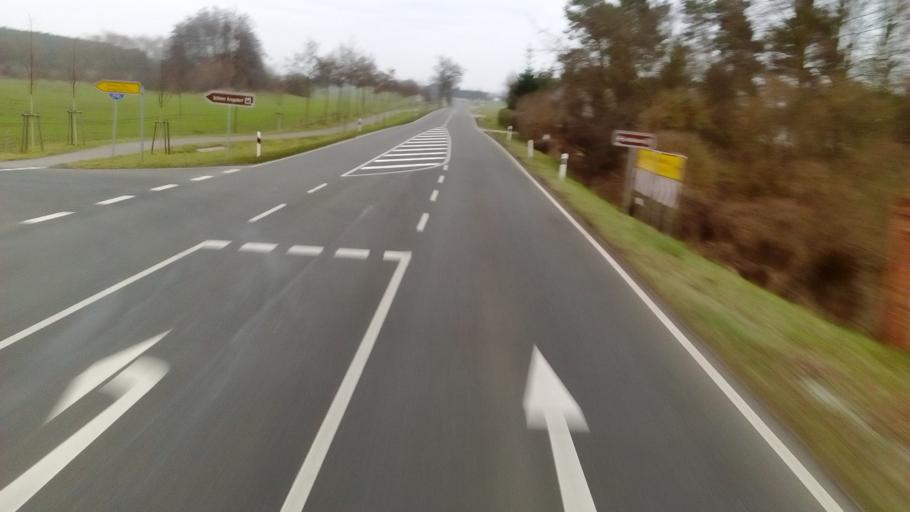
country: DE
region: Mecklenburg-Vorpommern
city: Viereck
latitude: 53.5037
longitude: 14.0408
